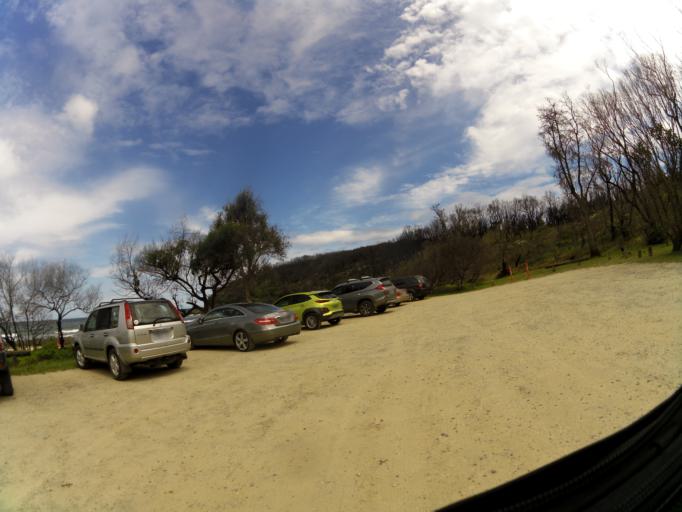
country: AU
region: Victoria
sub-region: East Gippsland
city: Lakes Entrance
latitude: -37.8024
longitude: 148.7412
